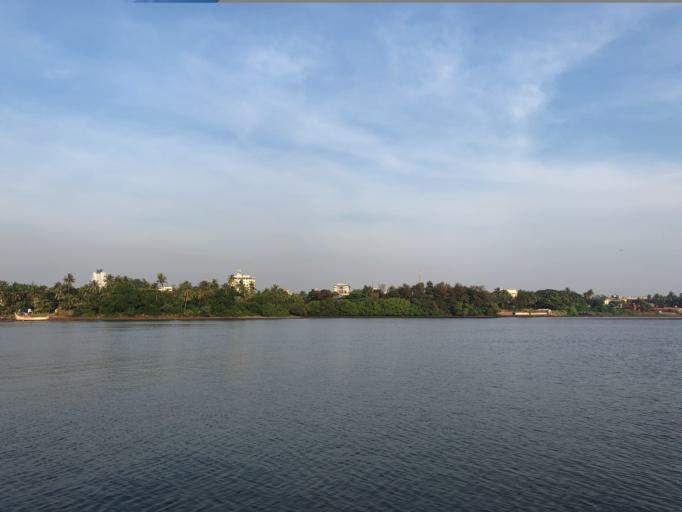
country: IN
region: Karnataka
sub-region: Dakshina Kannada
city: Mangalore
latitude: 12.8847
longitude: 74.8193
